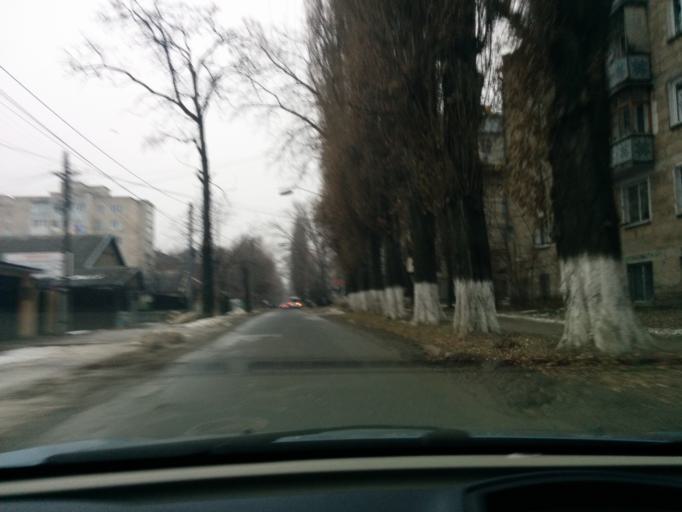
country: MD
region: Chisinau
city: Chisinau
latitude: 46.9976
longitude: 28.8643
